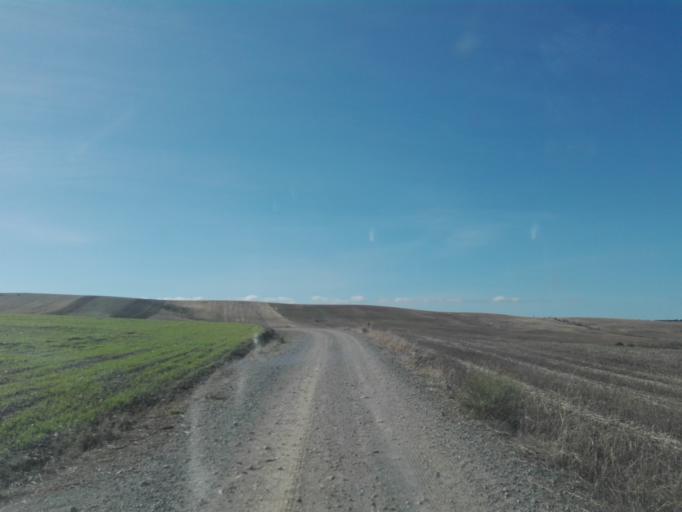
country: ES
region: Extremadura
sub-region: Provincia de Badajoz
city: Maguilla
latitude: 38.3331
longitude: -5.8954
